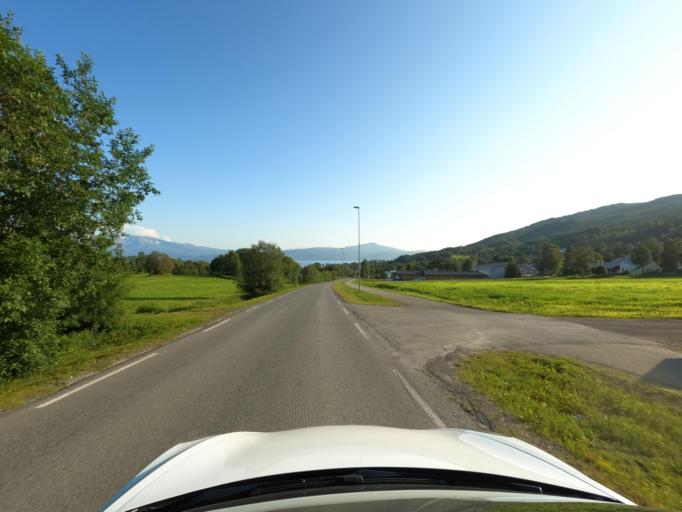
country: NO
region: Nordland
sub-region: Evenes
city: Randa
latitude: 68.4853
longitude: 16.8962
